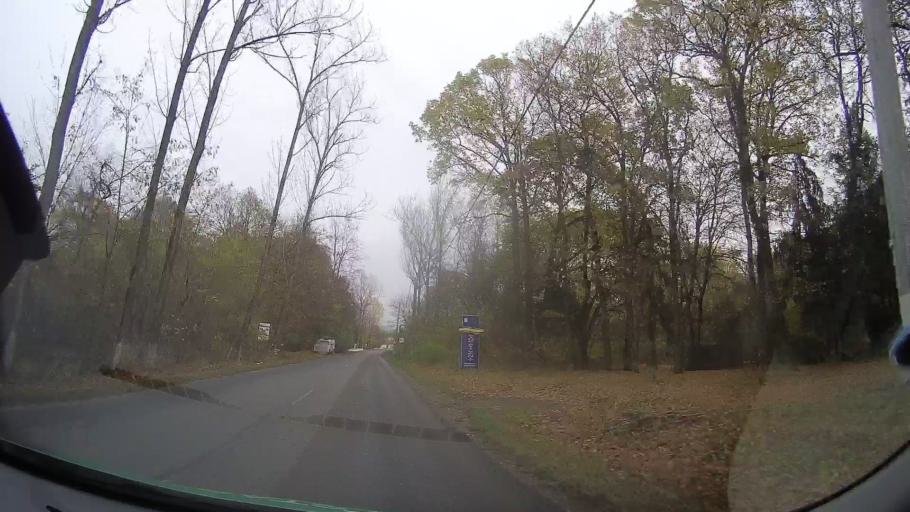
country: RO
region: Ilfov
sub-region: Comuna Gruiu
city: Gruiu
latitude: 44.7203
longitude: 26.2063
